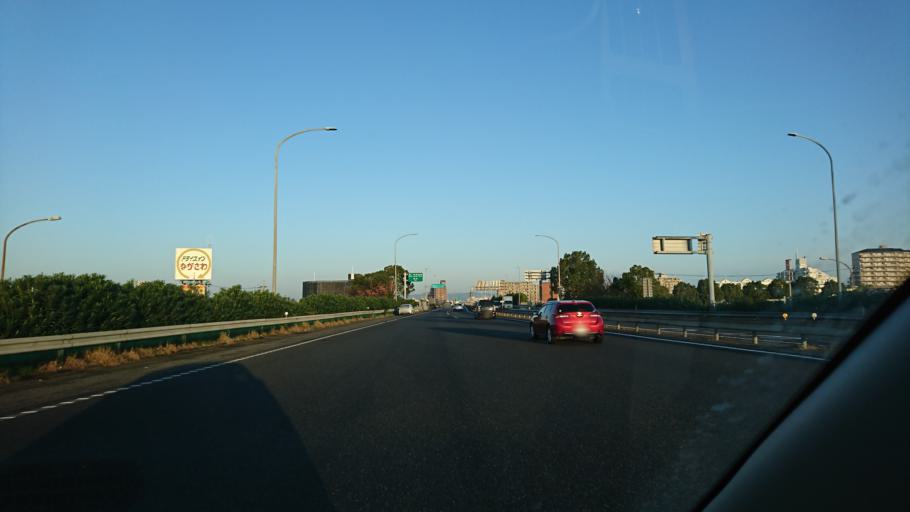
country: JP
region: Hyogo
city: Kakogawacho-honmachi
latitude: 34.7207
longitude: 134.8978
